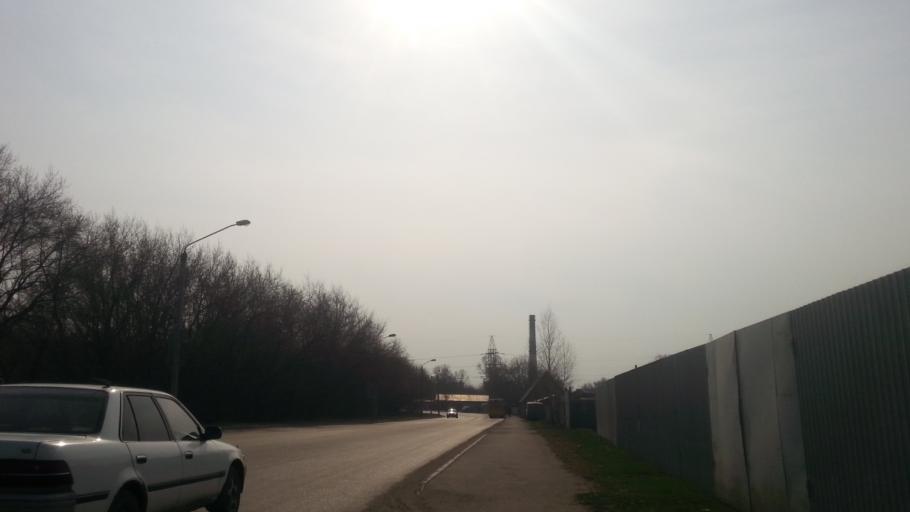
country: RU
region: Altai Krai
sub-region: Gorod Barnaulskiy
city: Barnaul
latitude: 53.3232
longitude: 83.7671
